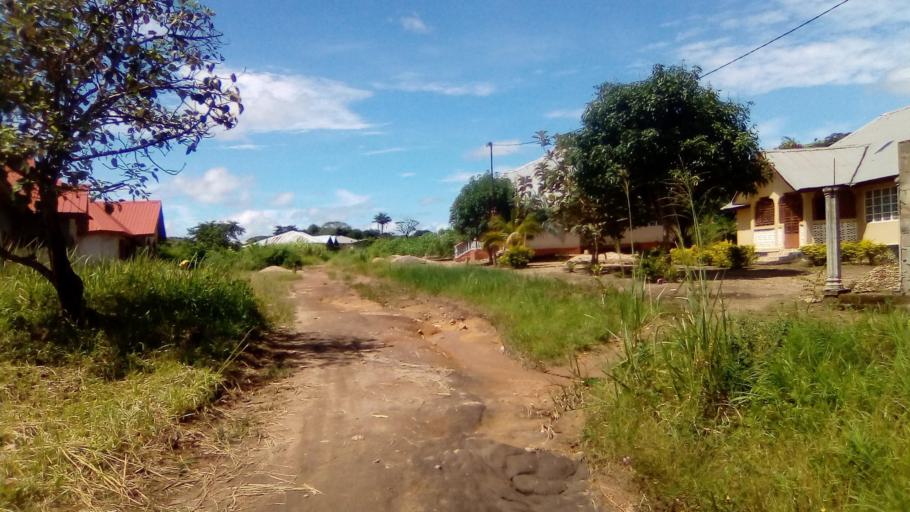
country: SL
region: Eastern Province
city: Simbakoro
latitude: 8.6344
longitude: -10.9982
